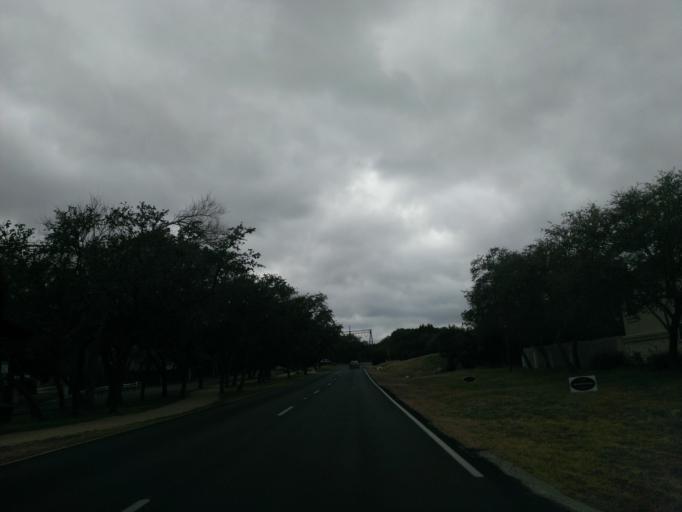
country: US
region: Texas
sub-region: Travis County
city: The Hills
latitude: 30.3539
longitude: -97.9910
